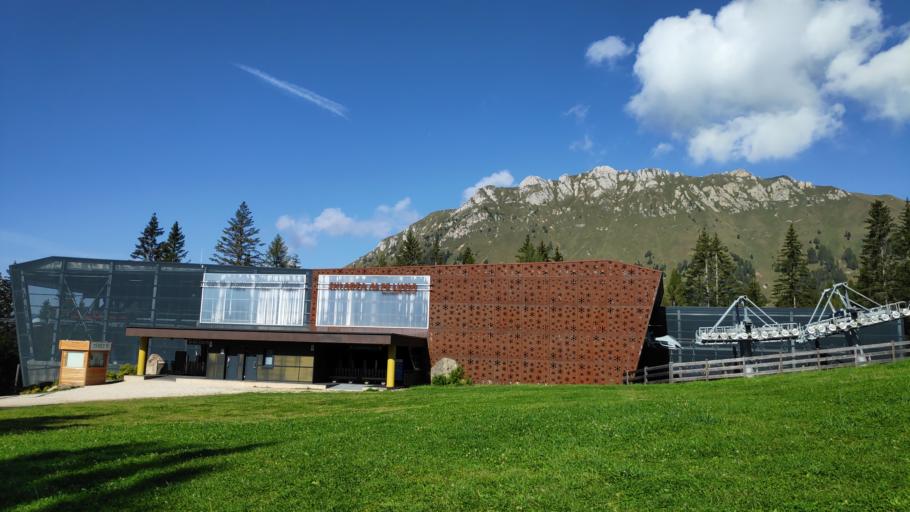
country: IT
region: Trentino-Alto Adige
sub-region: Provincia di Trento
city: Moena
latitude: 46.3242
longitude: 11.6990
